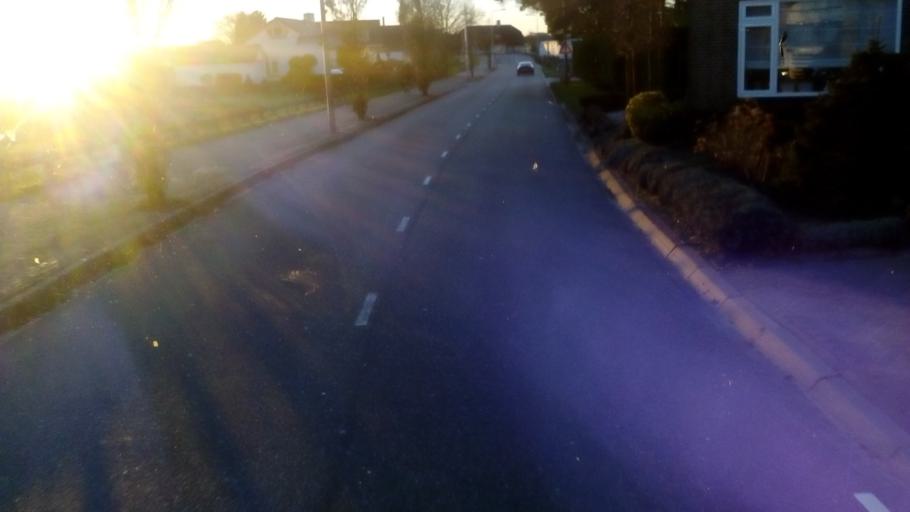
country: NL
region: South Holland
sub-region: Gemeente Westland
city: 's-Gravenzande
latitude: 52.0040
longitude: 4.1843
